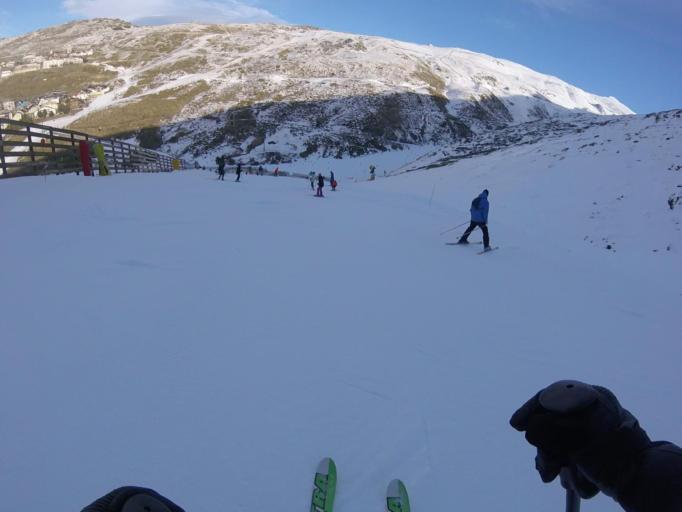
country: ES
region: Andalusia
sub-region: Provincia de Granada
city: Guejar-Sierra
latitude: 37.0883
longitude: -3.4011
